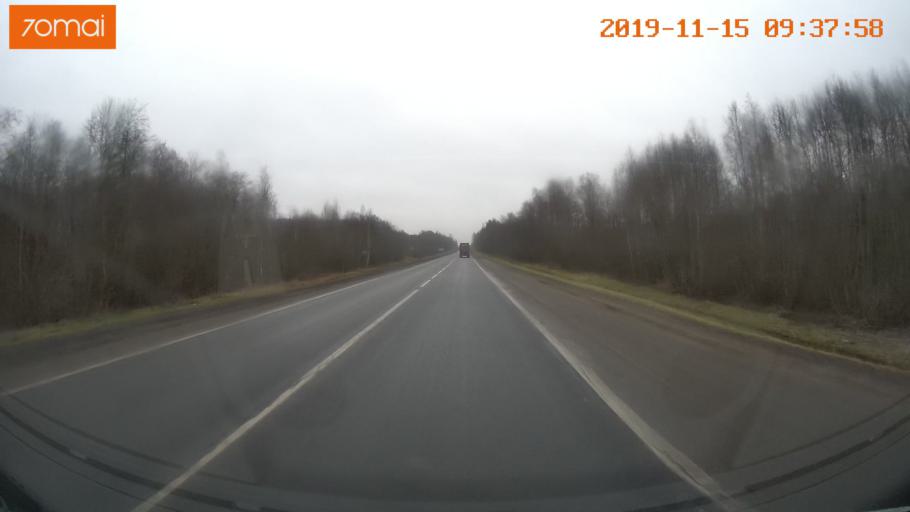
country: RU
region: Vologda
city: Sheksna
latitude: 59.2362
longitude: 38.4465
